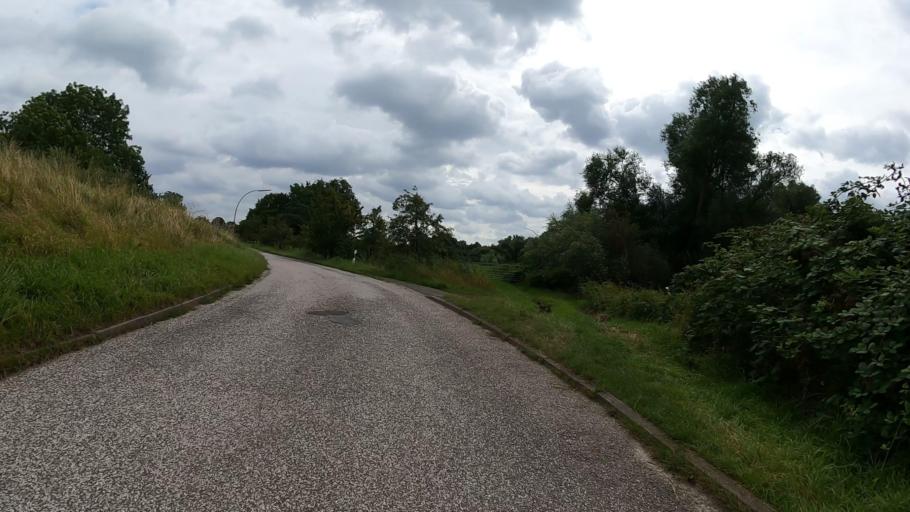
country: DE
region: Lower Saxony
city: Neu Wulmstorf
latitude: 53.5198
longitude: 9.8453
